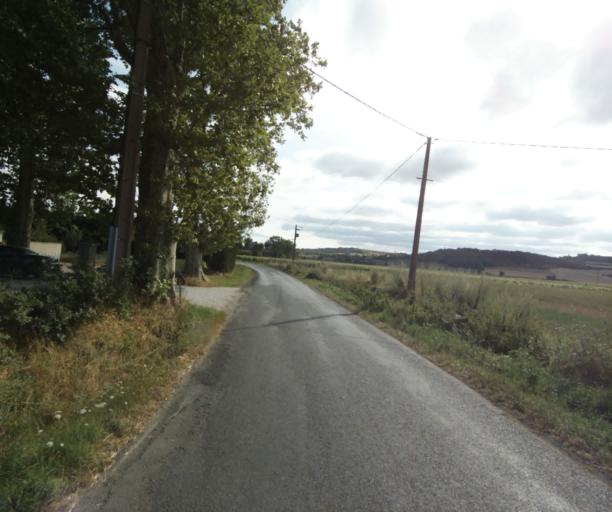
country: FR
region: Midi-Pyrenees
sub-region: Departement de la Haute-Garonne
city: Revel
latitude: 43.5178
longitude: 1.9607
